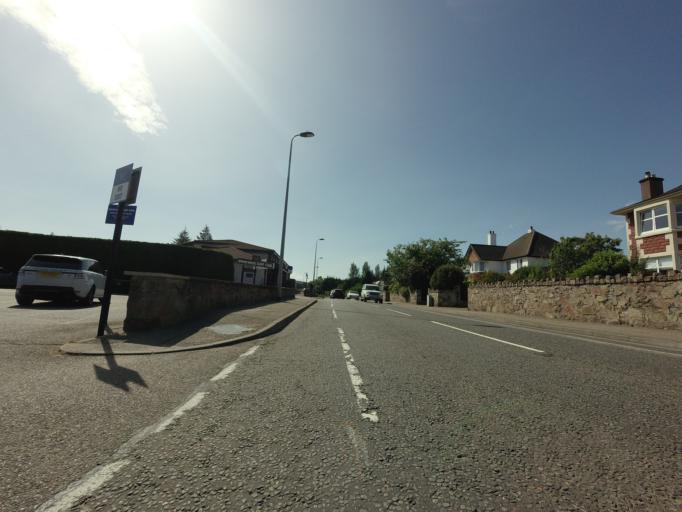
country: GB
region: Scotland
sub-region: Highland
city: Inverness
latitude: 57.4732
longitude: -4.2013
